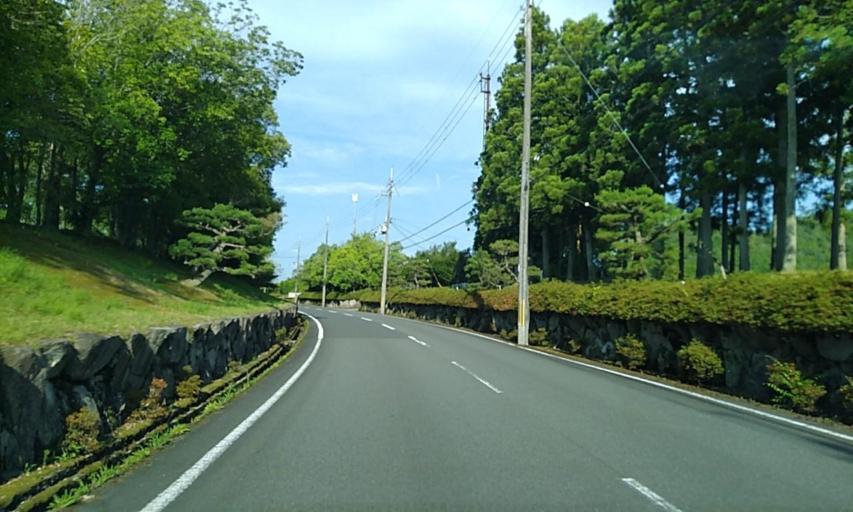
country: JP
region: Hyogo
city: Sasayama
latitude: 35.1625
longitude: 135.3686
